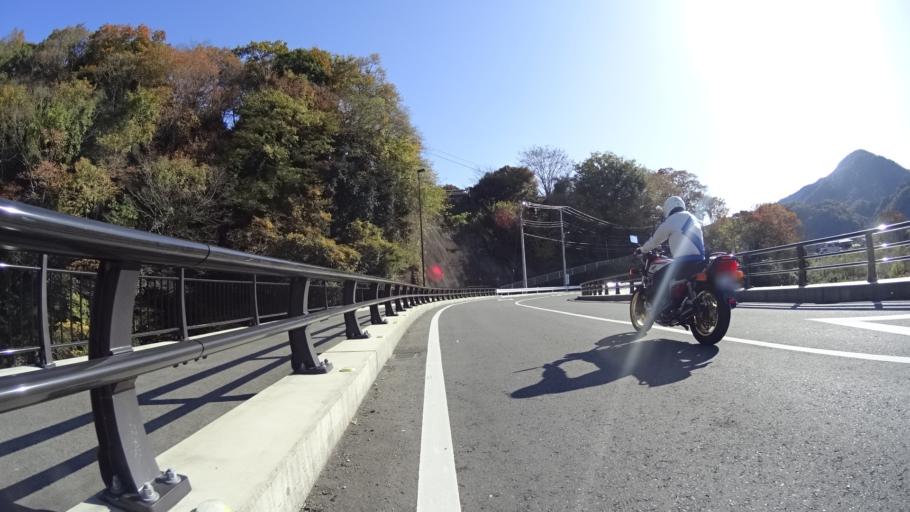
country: JP
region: Kanagawa
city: Zama
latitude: 35.5321
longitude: 139.2853
